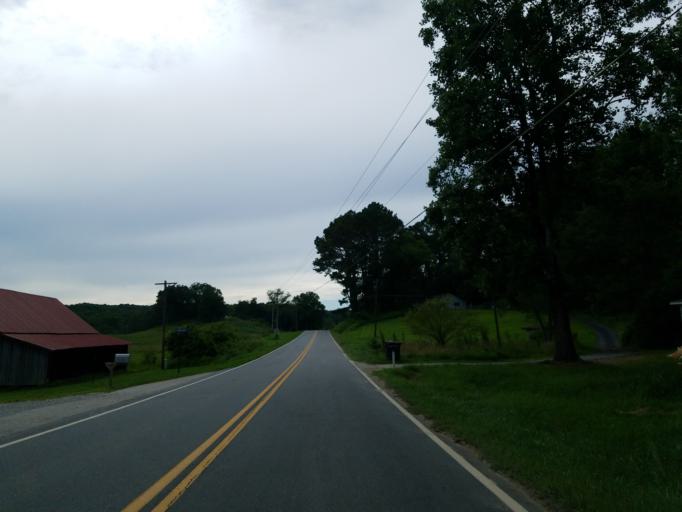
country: US
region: Georgia
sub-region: Lumpkin County
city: Dahlonega
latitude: 34.5633
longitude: -83.9513
